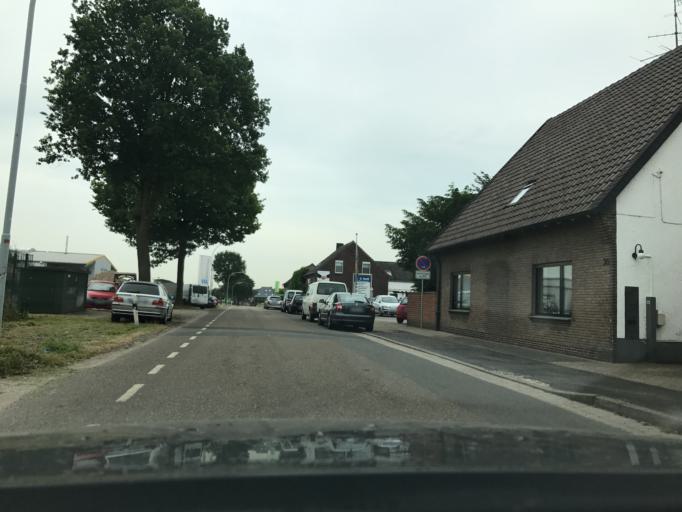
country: DE
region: North Rhine-Westphalia
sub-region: Regierungsbezirk Dusseldorf
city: Wachtendonk
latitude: 51.3961
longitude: 6.3092
